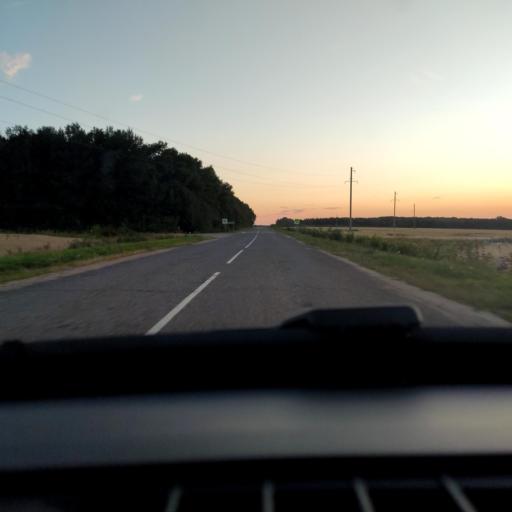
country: RU
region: Lipetsk
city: Zadonsk
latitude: 52.3103
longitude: 38.8918
